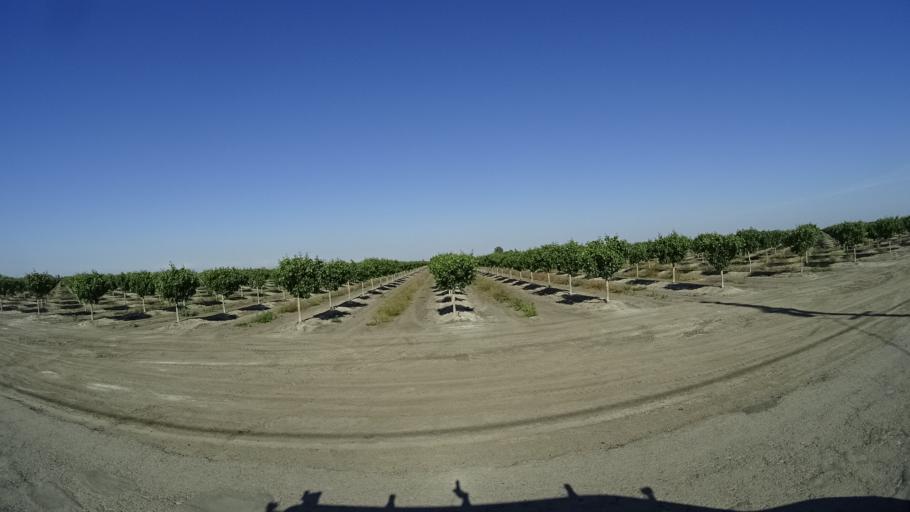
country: US
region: California
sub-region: Kings County
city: Corcoran
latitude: 36.1305
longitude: -119.5543
